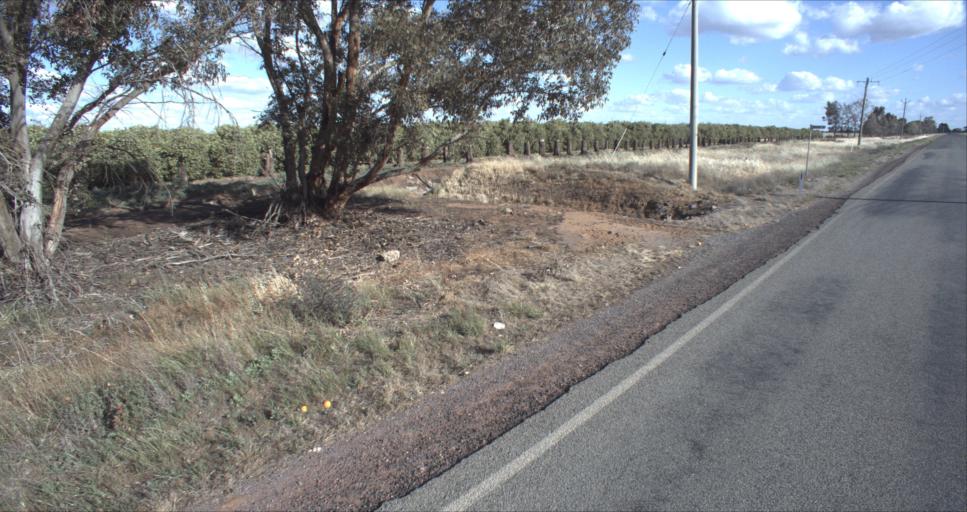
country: AU
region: New South Wales
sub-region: Leeton
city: Leeton
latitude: -34.5276
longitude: 146.2821
